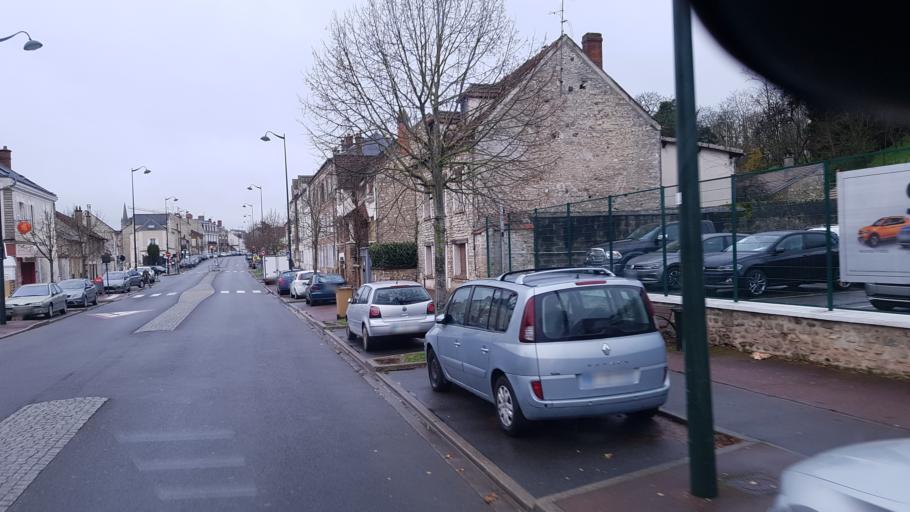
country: FR
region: Ile-de-France
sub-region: Departement de l'Essonne
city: Morigny-Champigny
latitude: 48.4403
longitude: 2.1692
